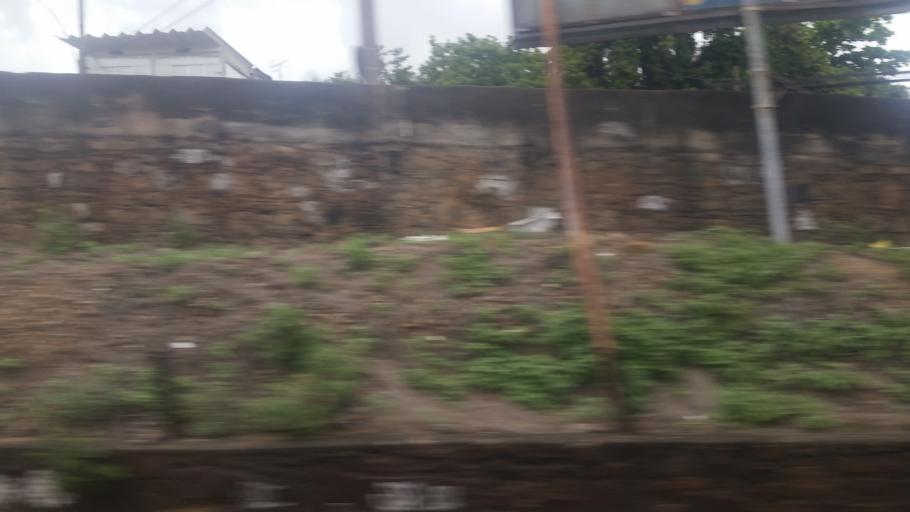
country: BR
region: Rio de Janeiro
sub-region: Rio De Janeiro
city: Rio de Janeiro
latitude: -22.8970
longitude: -43.2865
